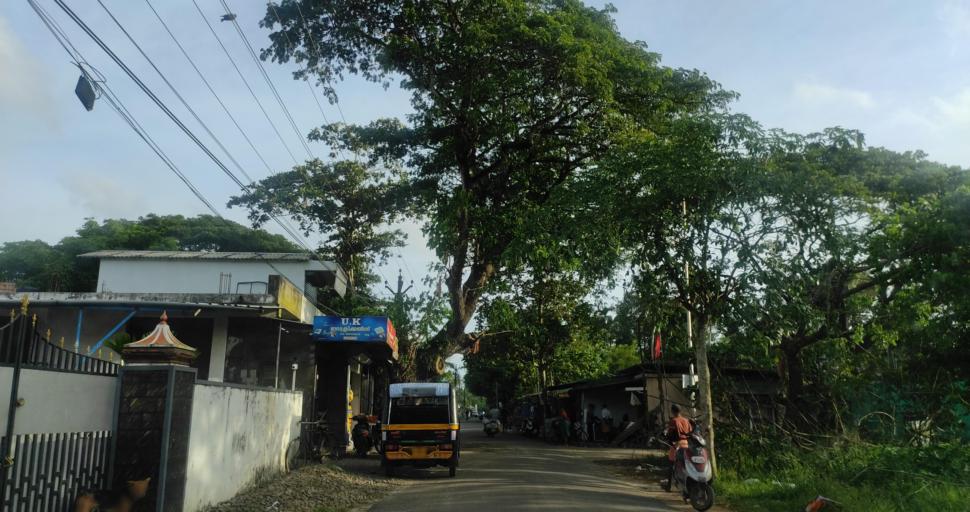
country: IN
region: Kerala
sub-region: Alappuzha
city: Shertallai
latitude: 9.6240
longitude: 76.3429
